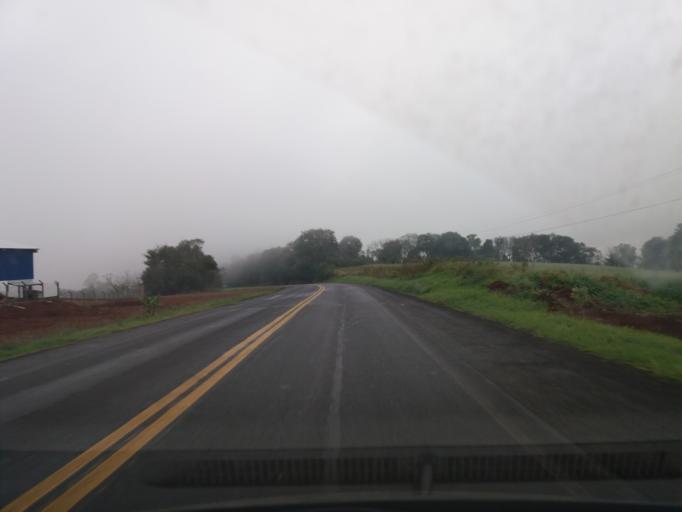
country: BR
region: Parana
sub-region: Ampere
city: Ampere
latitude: -25.8796
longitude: -53.4753
